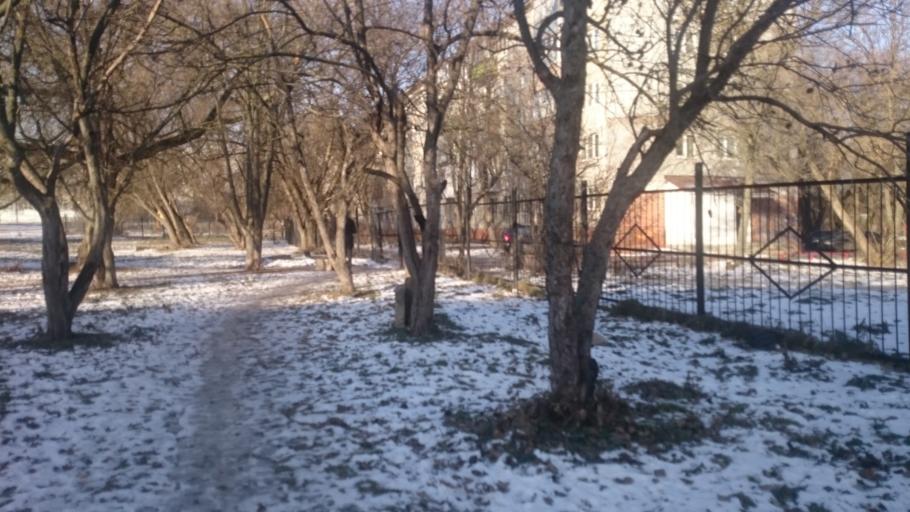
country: RU
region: Tula
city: Tula
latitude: 54.1764
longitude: 37.6387
